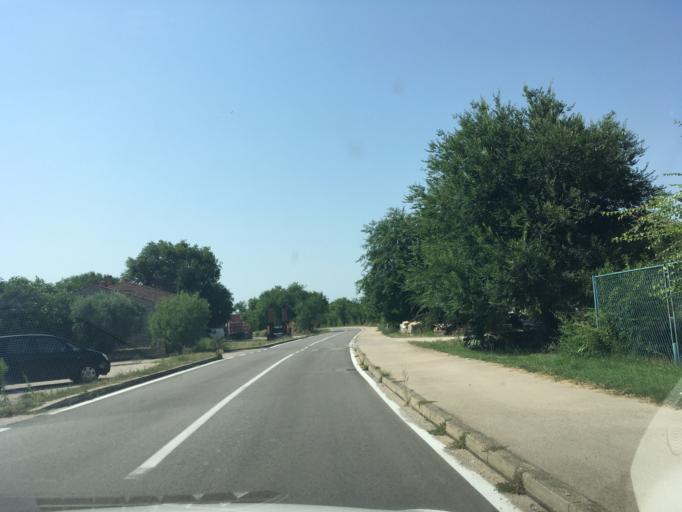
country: HR
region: Zadarska
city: Benkovac
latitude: 44.0261
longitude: 15.6154
